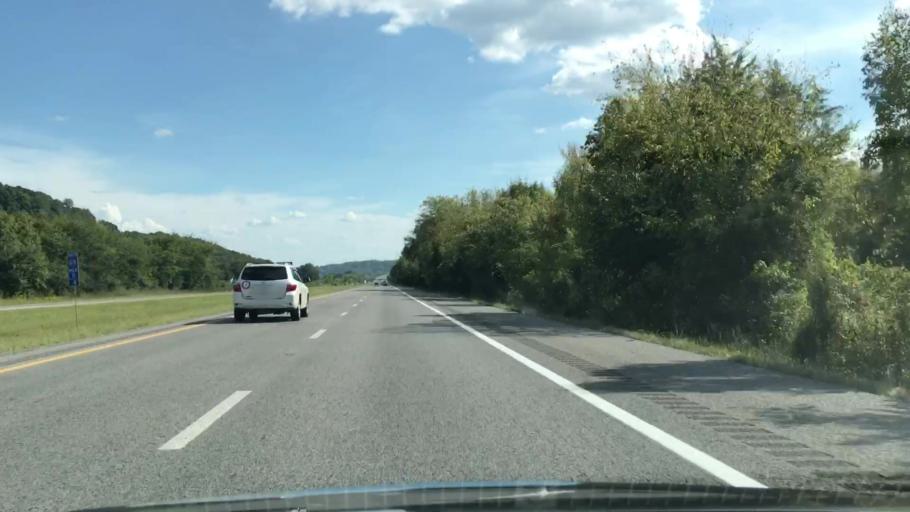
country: US
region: Tennessee
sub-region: Giles County
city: Pulaski
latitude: 35.1569
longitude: -86.8799
